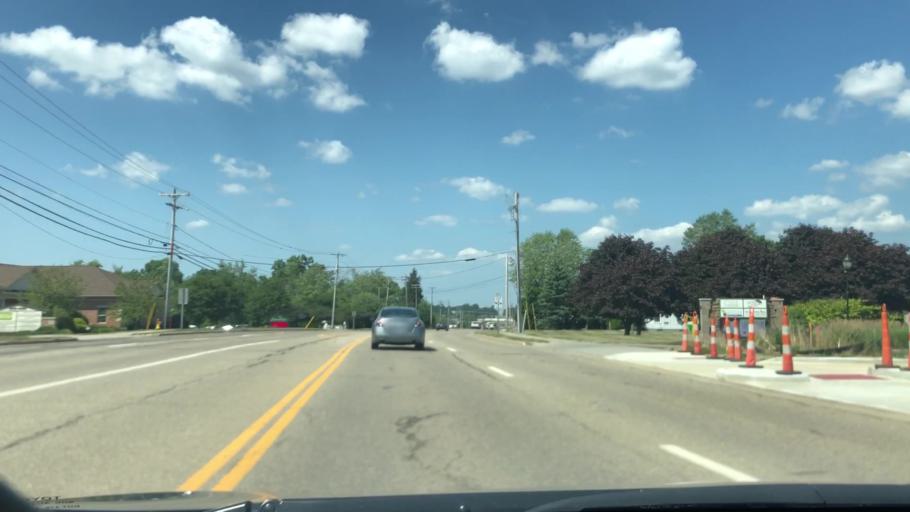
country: US
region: Ohio
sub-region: Summit County
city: Green
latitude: 40.9513
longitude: -81.4657
